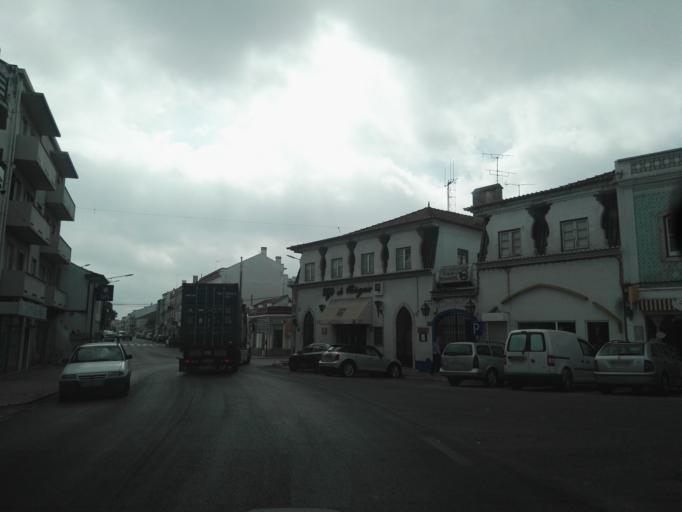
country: PT
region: Santarem
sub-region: Benavente
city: Benavente
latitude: 38.9821
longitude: -8.8080
